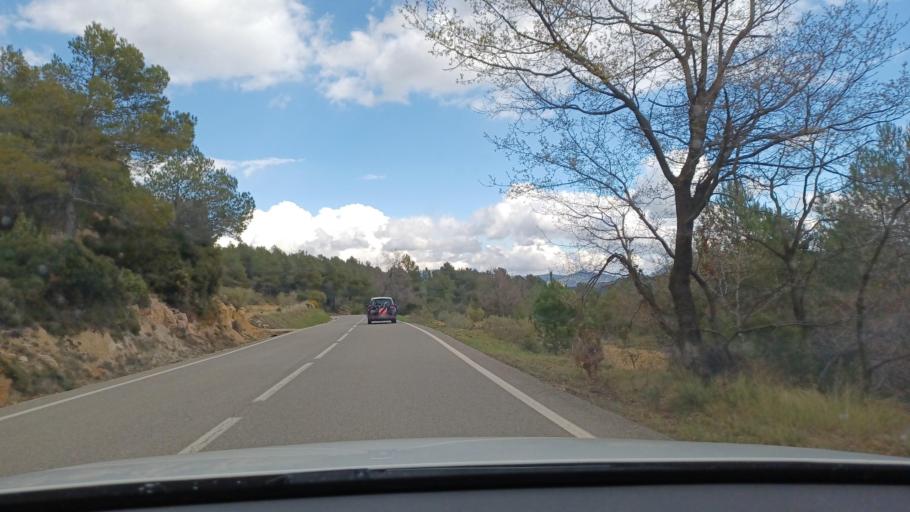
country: ES
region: Catalonia
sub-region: Provincia de Tarragona
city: la Morera de Montsant
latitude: 41.2699
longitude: 0.8570
